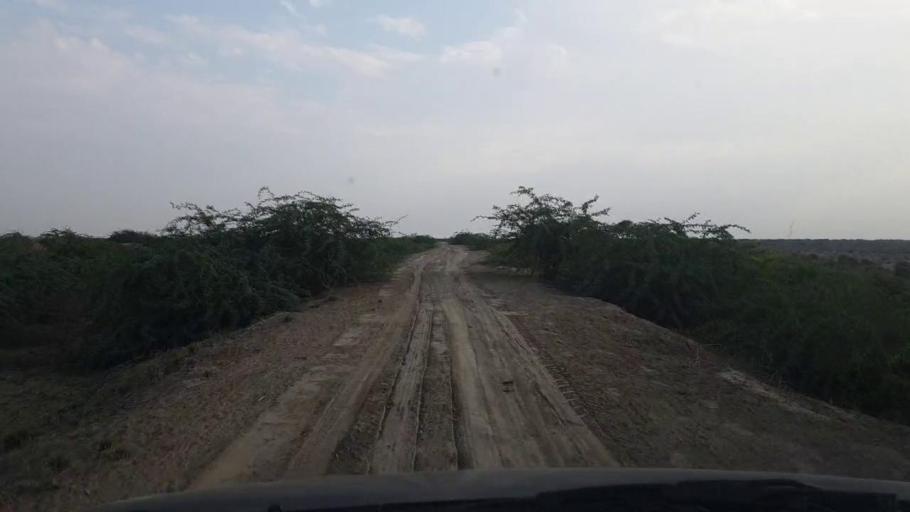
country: PK
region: Sindh
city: Badin
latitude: 24.4794
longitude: 68.6992
